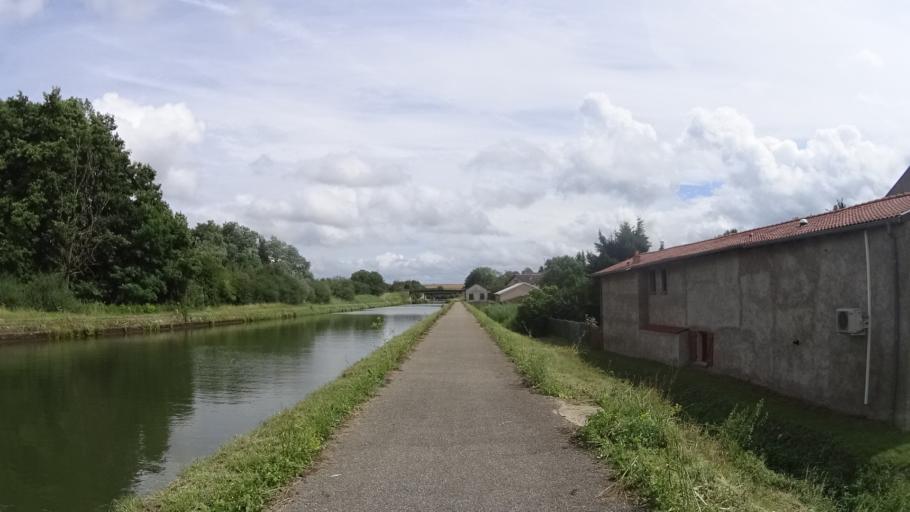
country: FR
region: Lorraine
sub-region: Departement de la Moselle
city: Lorquin
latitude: 48.6856
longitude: 6.9304
